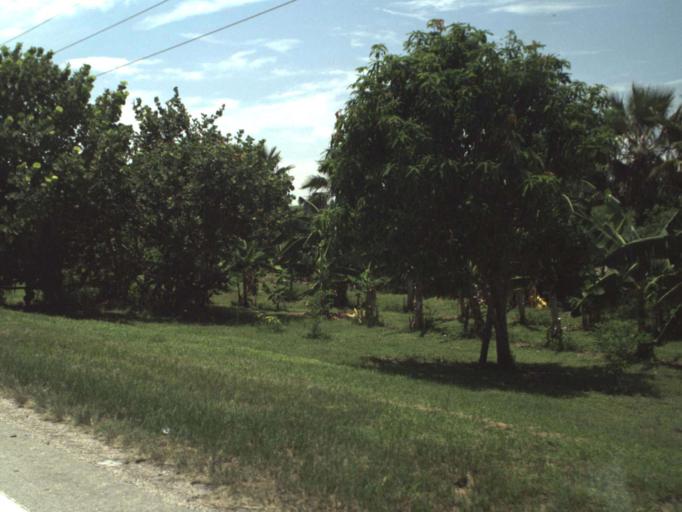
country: US
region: Florida
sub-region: Palm Beach County
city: Pahokee
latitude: 26.8728
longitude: -80.6247
